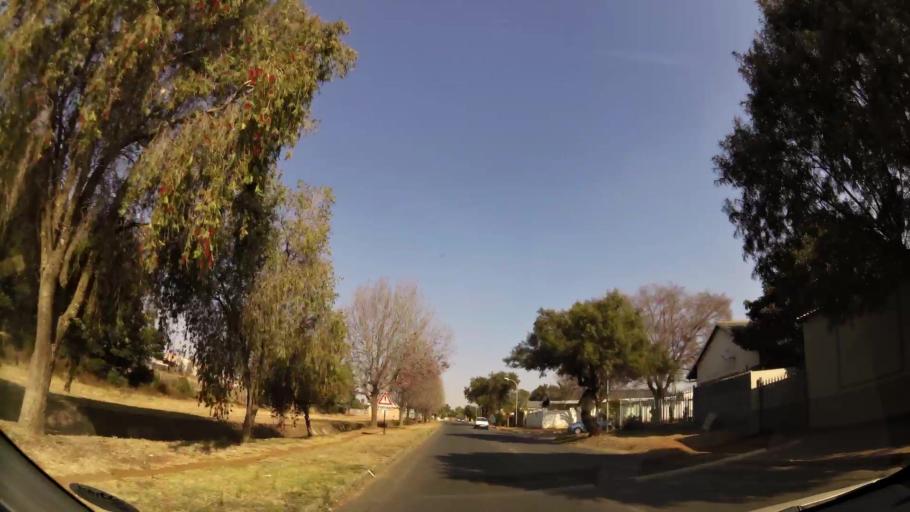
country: ZA
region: Gauteng
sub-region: West Rand District Municipality
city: Randfontein
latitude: -26.1703
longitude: 27.6893
